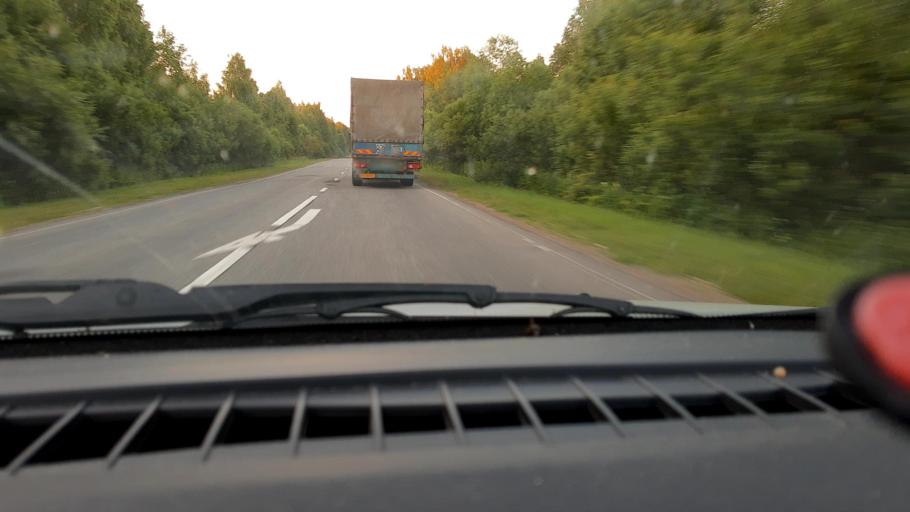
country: RU
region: Nizjnij Novgorod
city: Uren'
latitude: 57.3139
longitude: 45.6871
